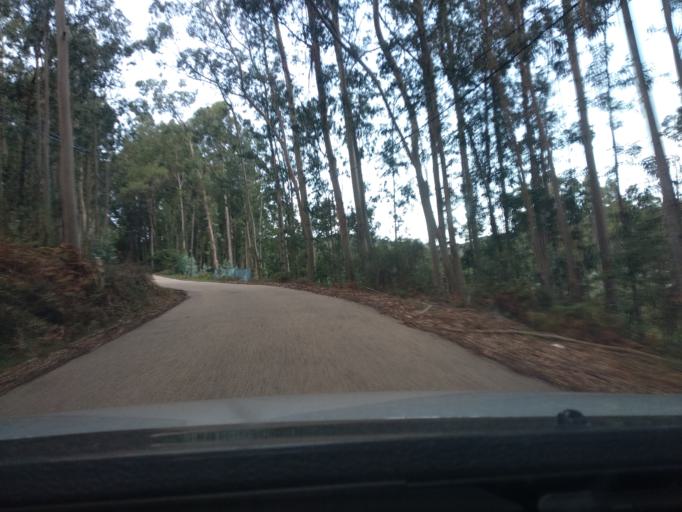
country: ES
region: Galicia
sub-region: Provincia de Pontevedra
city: Moana
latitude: 42.2988
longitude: -8.6953
